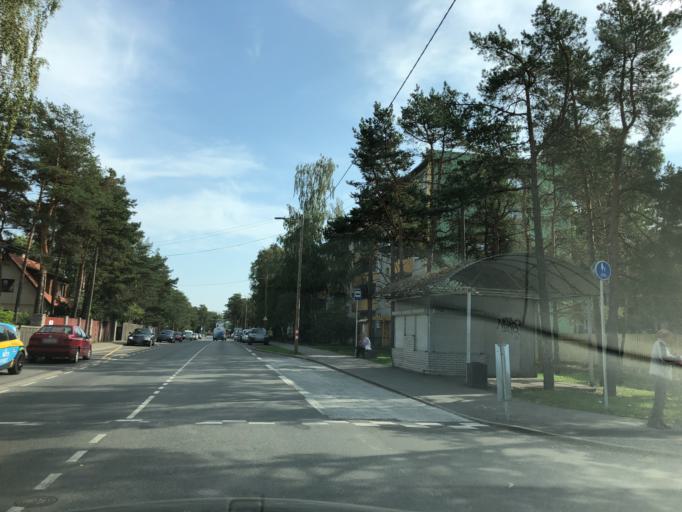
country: EE
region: Harju
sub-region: Tallinna linn
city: Tallinn
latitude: 59.3763
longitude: 24.7126
